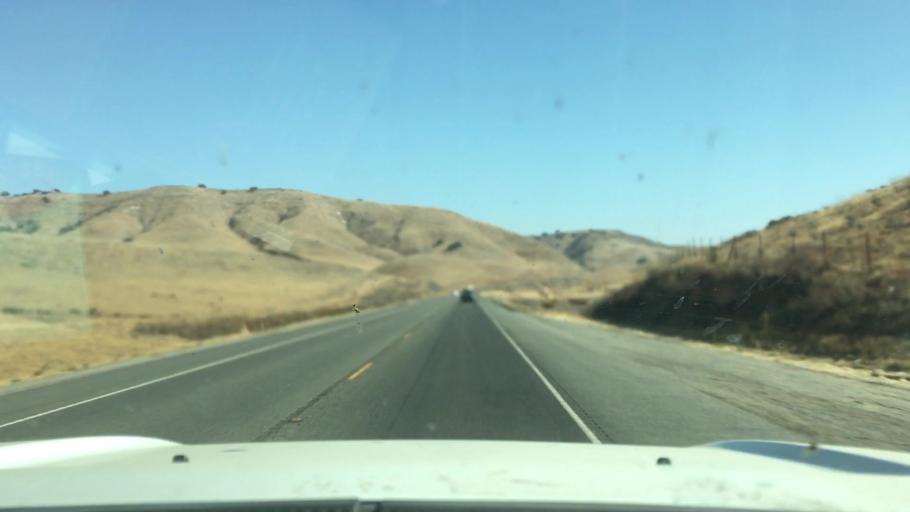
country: US
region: California
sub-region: San Luis Obispo County
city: Shandon
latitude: 35.7434
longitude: -120.2308
